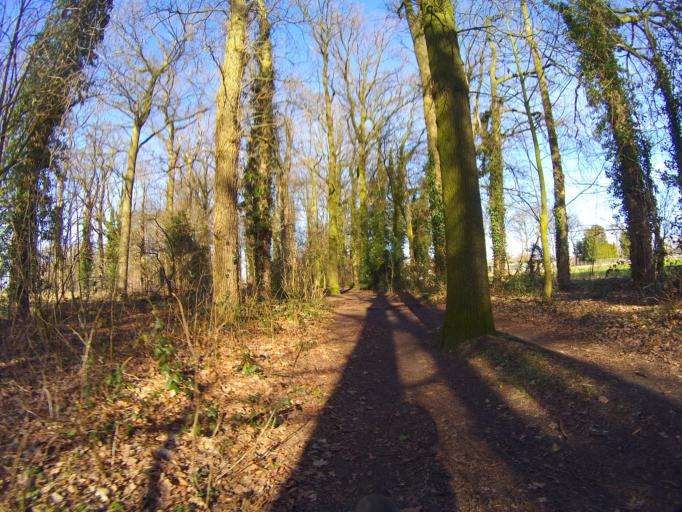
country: NL
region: Utrecht
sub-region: Gemeente Utrechtse Heuvelrug
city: Overberg
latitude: 52.0734
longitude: 5.4903
